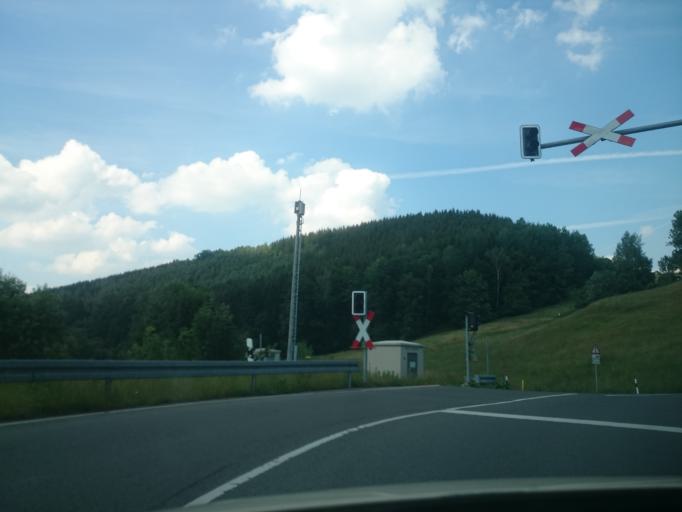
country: DE
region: Saxony
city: Lengefeld
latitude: 50.7309
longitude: 13.2021
